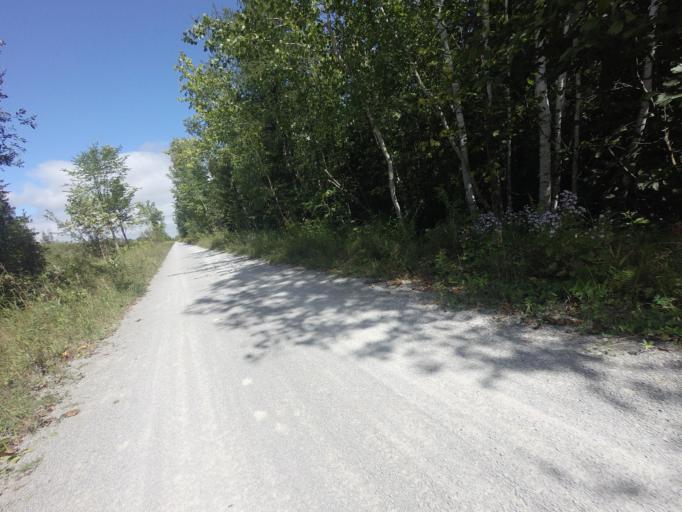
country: CA
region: Ontario
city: Uxbridge
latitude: 44.1334
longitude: -79.0945
